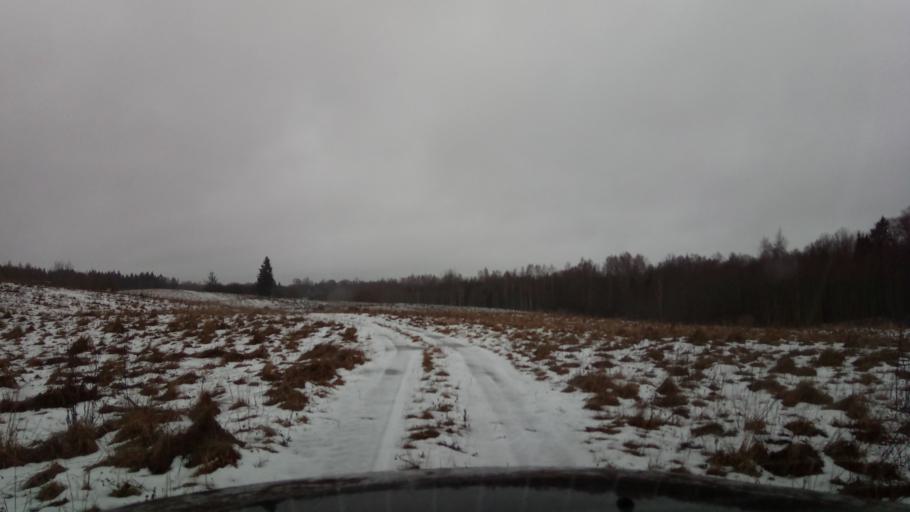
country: LT
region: Utenos apskritis
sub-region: Utena
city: Utena
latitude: 55.3654
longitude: 25.8091
